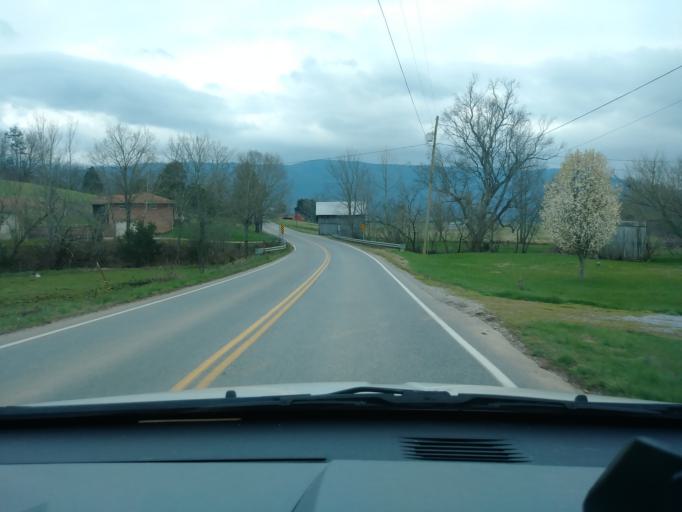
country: US
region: Tennessee
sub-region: Greene County
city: Tusculum
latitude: 36.0948
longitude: -82.7608
